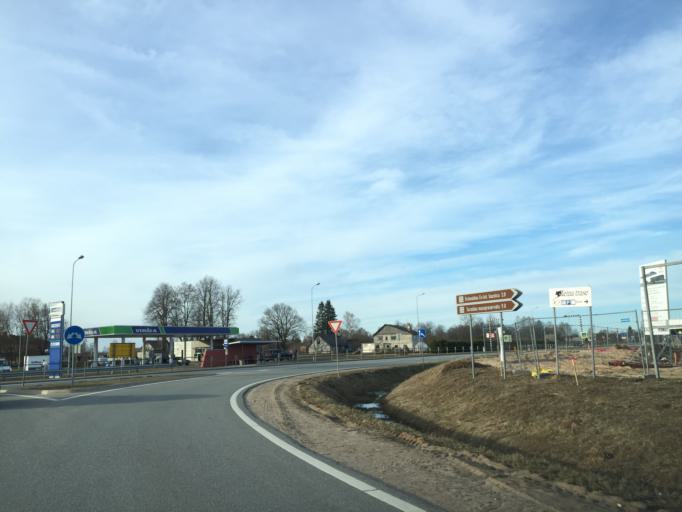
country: LV
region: Krimulda
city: Ragana
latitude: 57.1788
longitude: 24.7146
